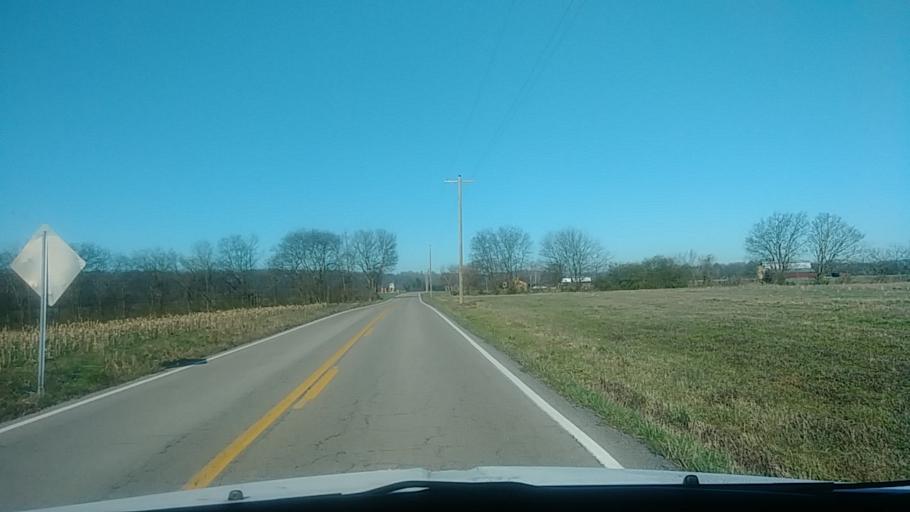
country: US
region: Tennessee
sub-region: Jefferson County
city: White Pine
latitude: 36.1501
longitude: -83.1527
